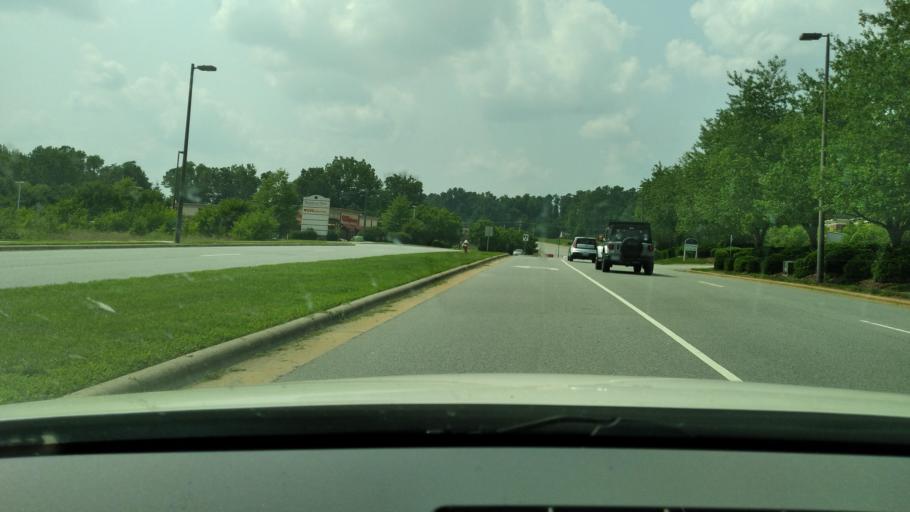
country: US
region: North Carolina
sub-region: Guilford County
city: Jamestown
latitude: 36.0435
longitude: -79.9252
